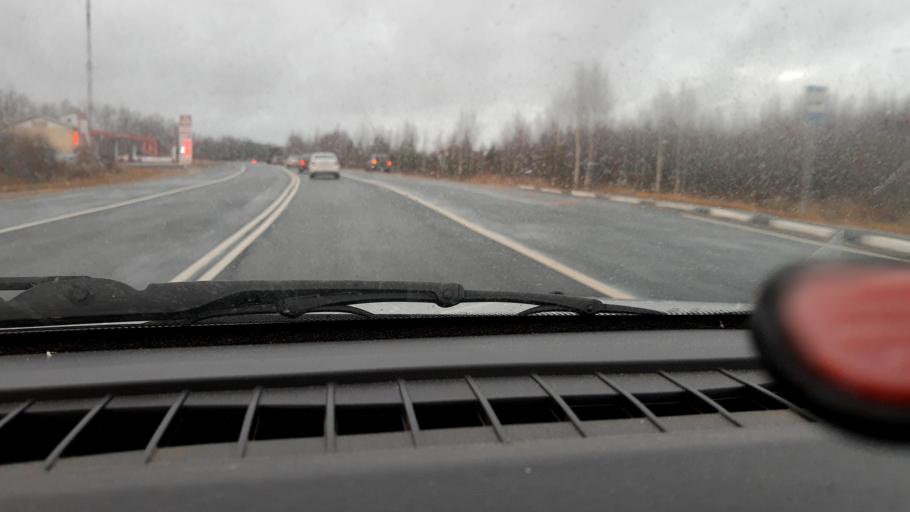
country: RU
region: Nizjnij Novgorod
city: Krasnyye Baki
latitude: 57.0851
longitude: 45.1473
